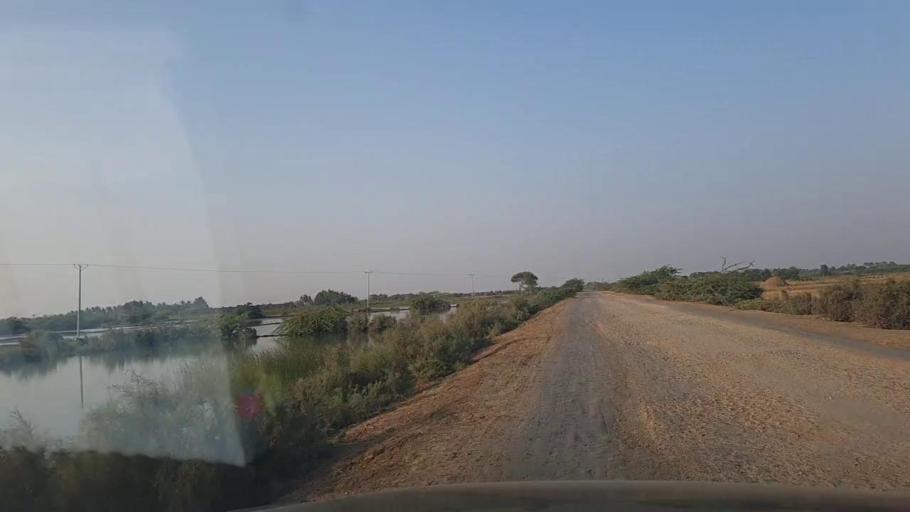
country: PK
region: Sindh
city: Keti Bandar
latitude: 24.2780
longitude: 67.5876
